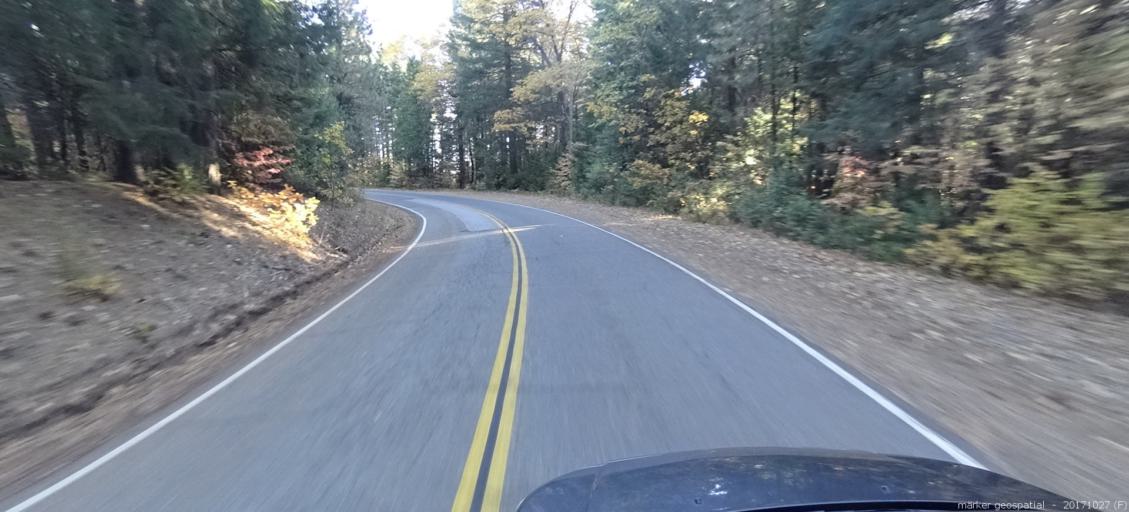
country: US
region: California
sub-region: Shasta County
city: Burney
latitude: 40.9690
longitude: -121.9305
